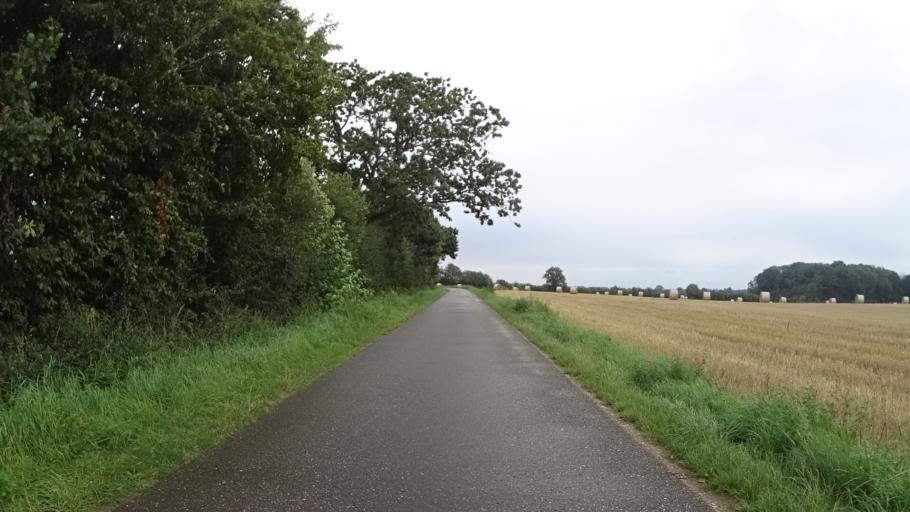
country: DE
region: Schleswig-Holstein
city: Stubben
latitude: 53.7144
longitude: 10.4368
